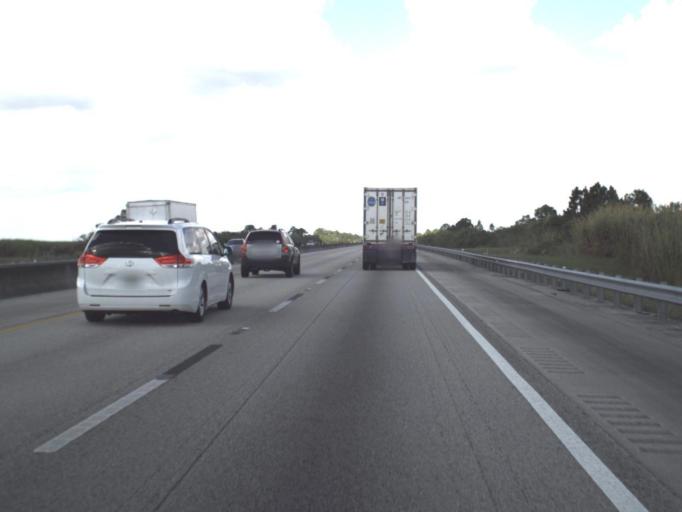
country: US
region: Florida
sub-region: Martin County
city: Hobe Sound
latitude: 27.0114
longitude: -80.2152
